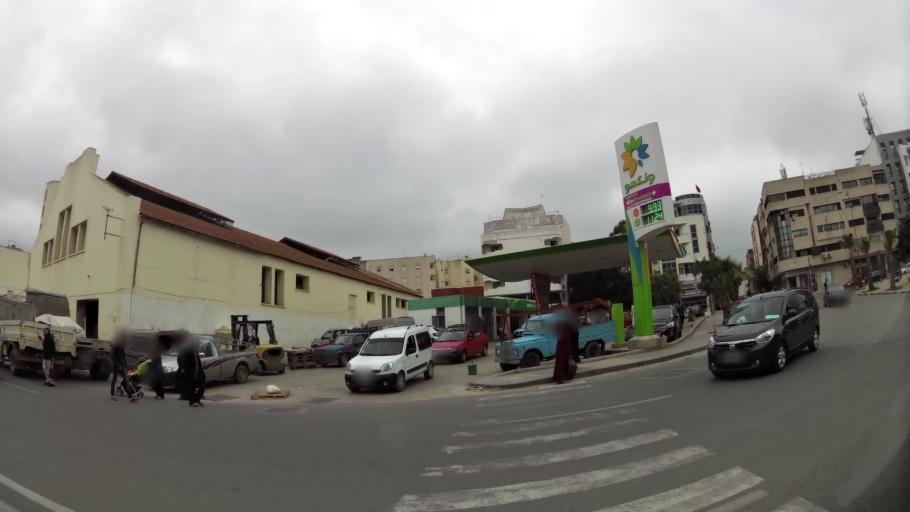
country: MA
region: Fes-Boulemane
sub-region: Fes
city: Fes
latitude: 34.0328
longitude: -4.9953
